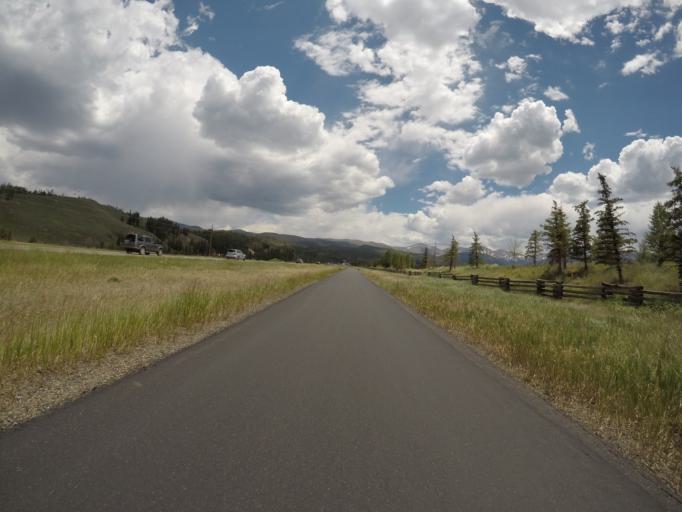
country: US
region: Colorado
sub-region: Grand County
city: Fraser
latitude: 39.9384
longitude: -105.8006
